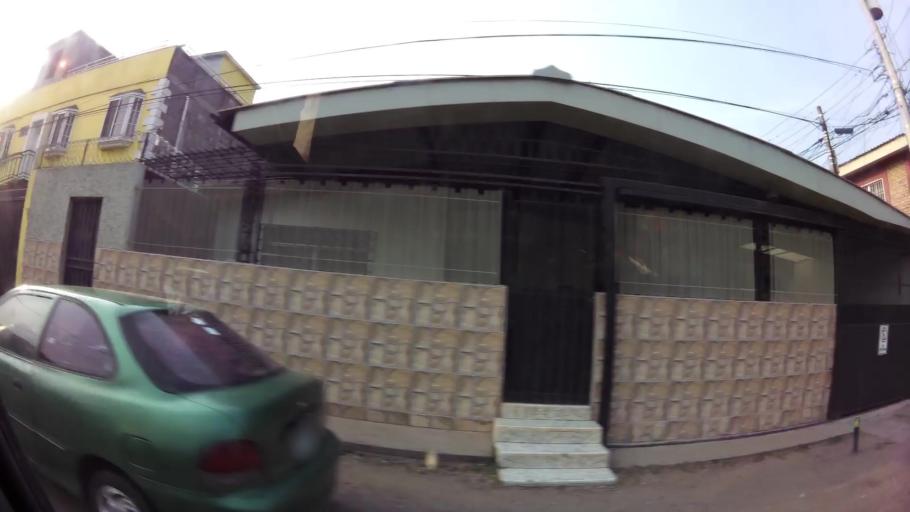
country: HN
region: Francisco Morazan
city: El Tablon
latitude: 14.0659
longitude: -87.1764
